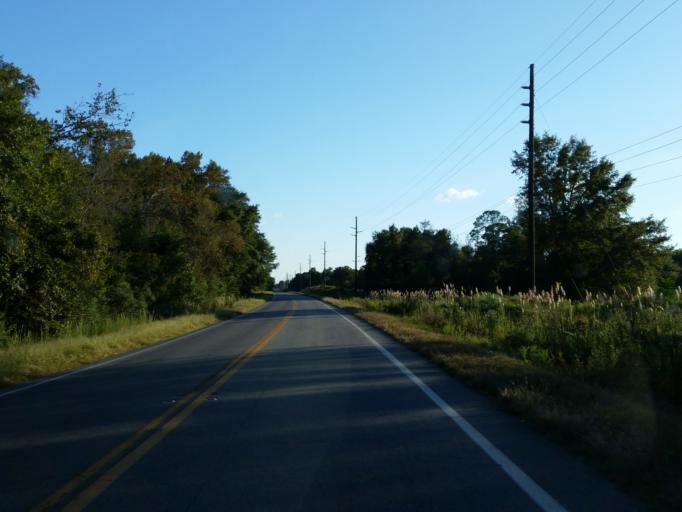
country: US
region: Georgia
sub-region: Dooly County
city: Vienna
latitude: 32.1081
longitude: -83.7765
